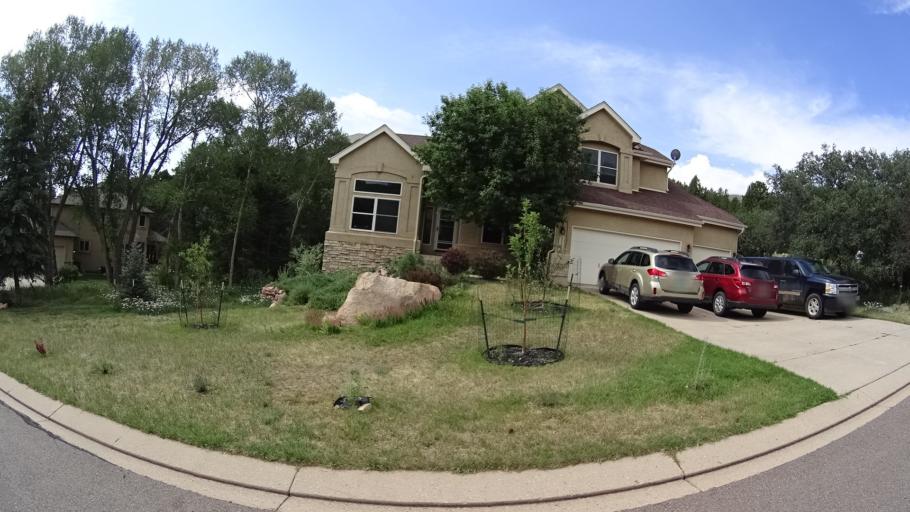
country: US
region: Colorado
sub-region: El Paso County
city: Air Force Academy
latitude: 38.9523
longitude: -104.8873
